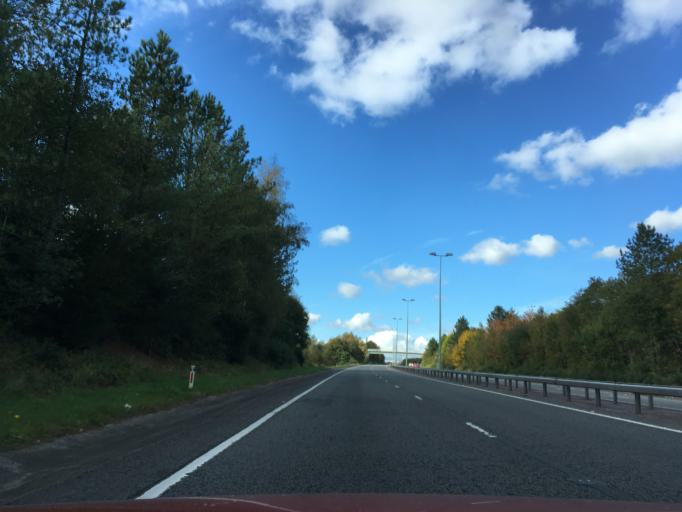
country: GB
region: Wales
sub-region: Merthyr Tydfil County Borough
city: Merthyr Tydfil
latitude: 51.7412
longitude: -3.3869
